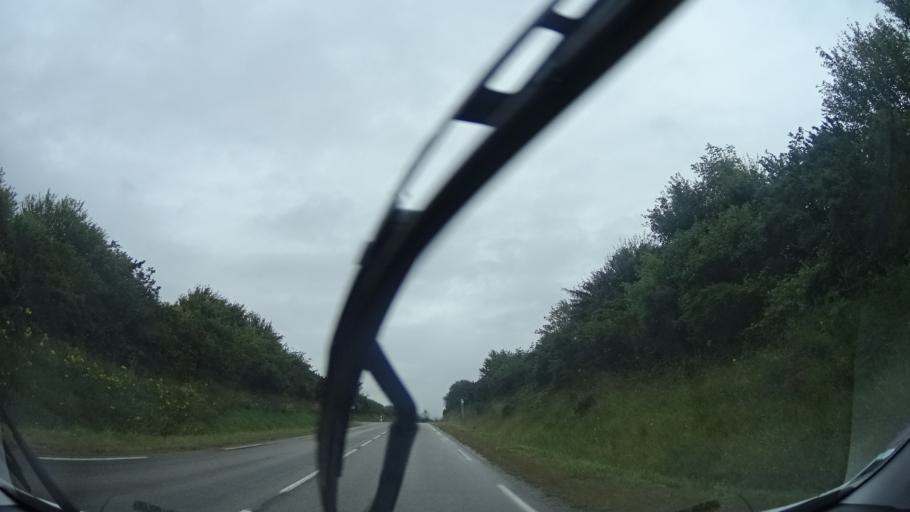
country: FR
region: Lower Normandy
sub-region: Departement de la Manche
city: Martinvast
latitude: 49.6054
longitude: -1.7325
